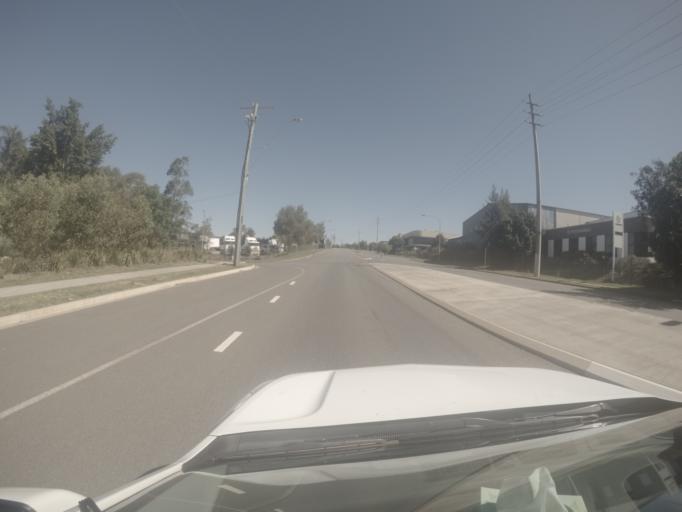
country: AU
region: Queensland
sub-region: Brisbane
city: Wacol
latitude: -27.5888
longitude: 152.9360
